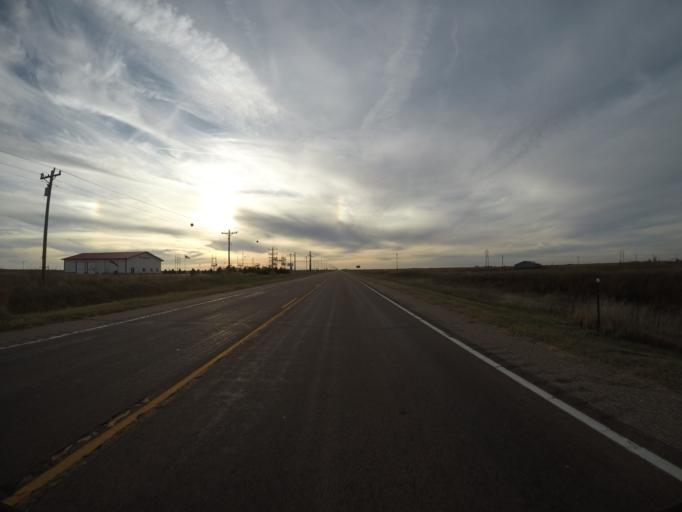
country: US
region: Colorado
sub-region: Yuma County
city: Yuma
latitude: 39.6560
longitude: -102.7049
